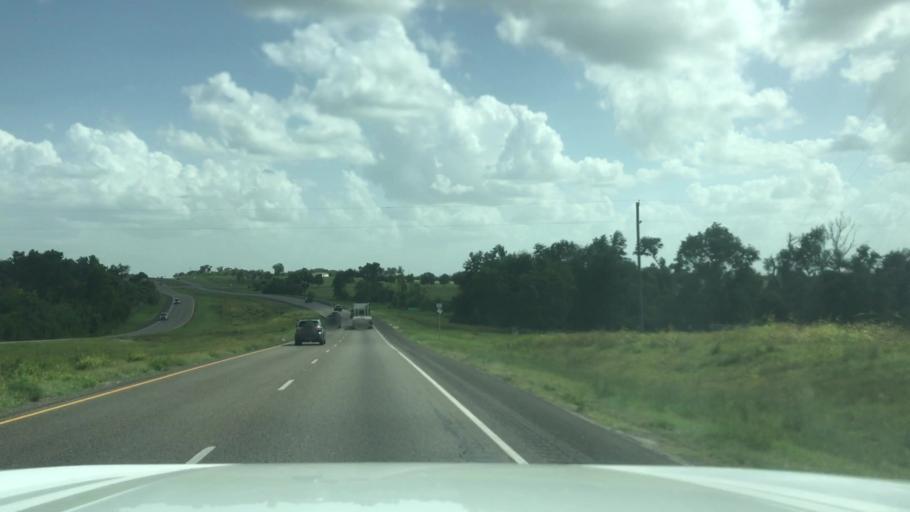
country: US
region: Texas
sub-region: Grimes County
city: Navasota
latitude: 30.3145
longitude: -96.0478
